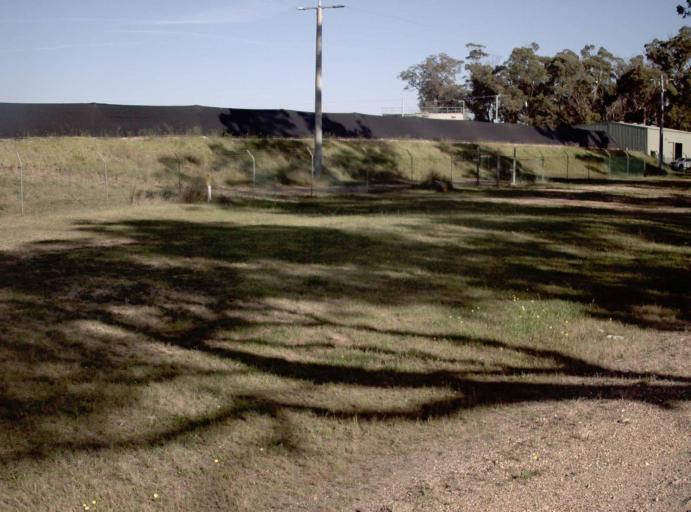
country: AU
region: Victoria
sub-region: East Gippsland
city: Lakes Entrance
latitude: -37.6916
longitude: 148.4688
